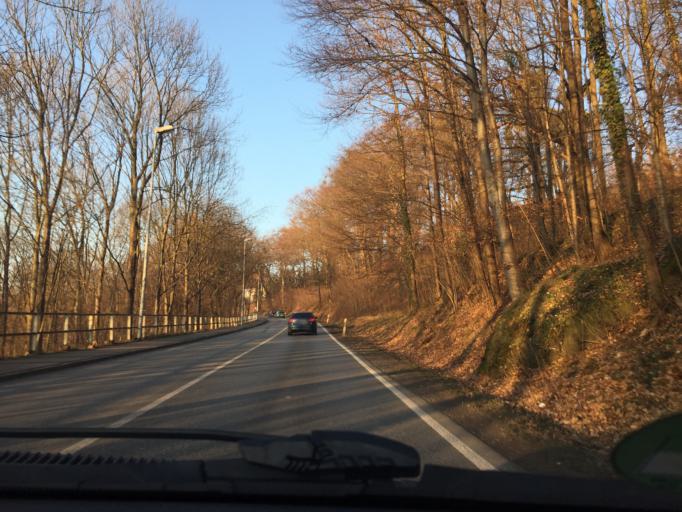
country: DE
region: Saxony
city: Pirna
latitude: 50.9569
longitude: 13.9453
